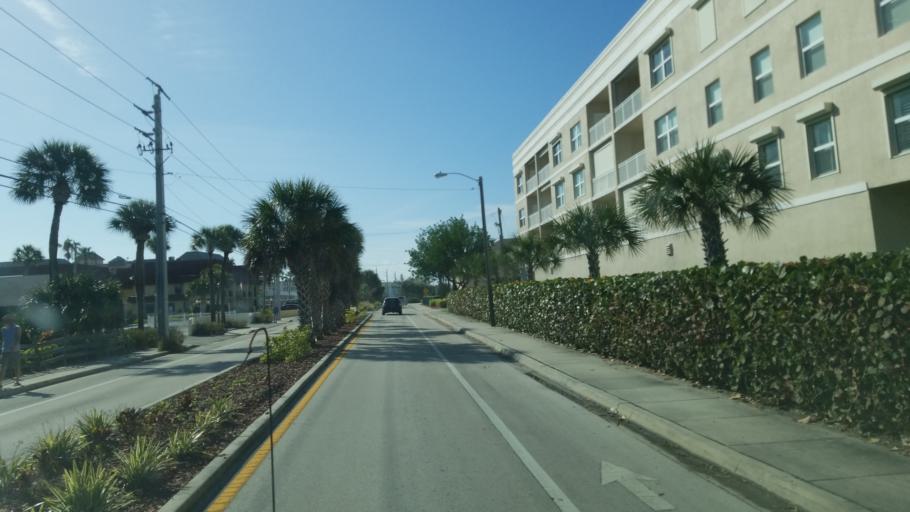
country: US
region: Florida
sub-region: Brevard County
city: Cape Canaveral
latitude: 28.3670
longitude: -80.6043
